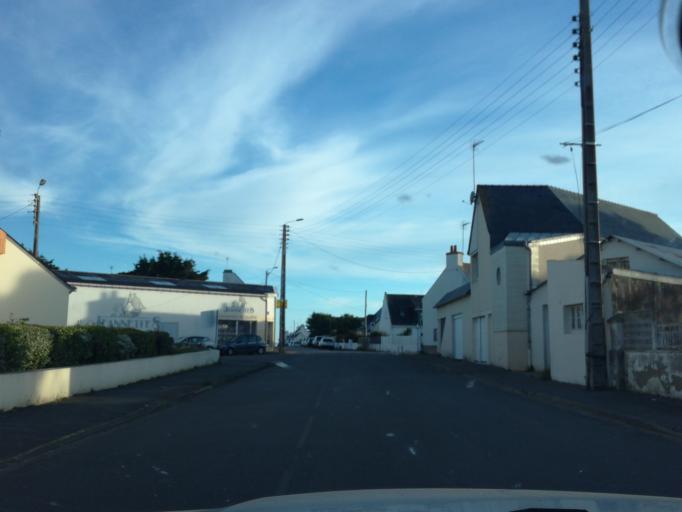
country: FR
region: Brittany
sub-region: Departement du Morbihan
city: Quiberon
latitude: 47.4781
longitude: -3.1283
